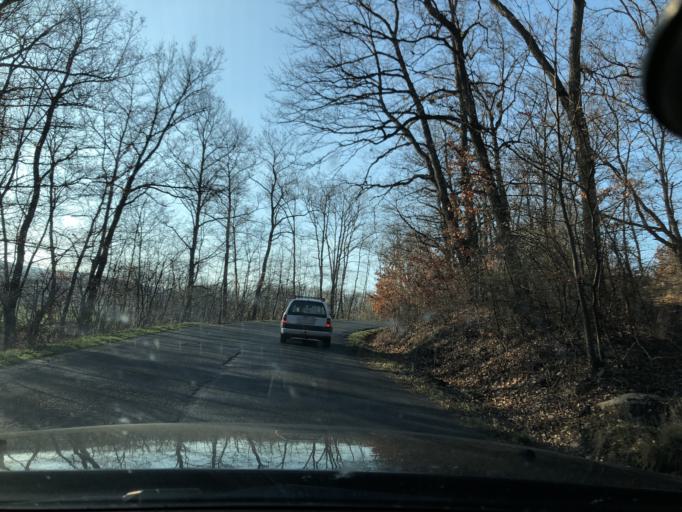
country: HU
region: Nograd
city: Paszto
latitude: 47.9290
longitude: 19.6286
